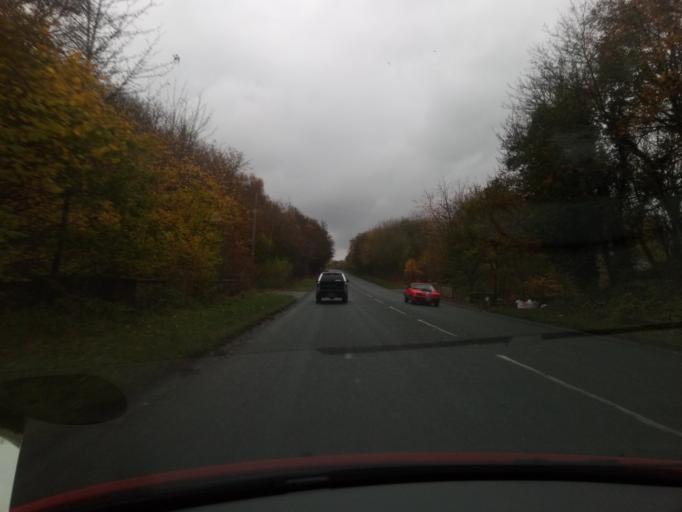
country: GB
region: England
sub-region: County Durham
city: High Etherley
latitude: 54.6651
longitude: -1.7729
